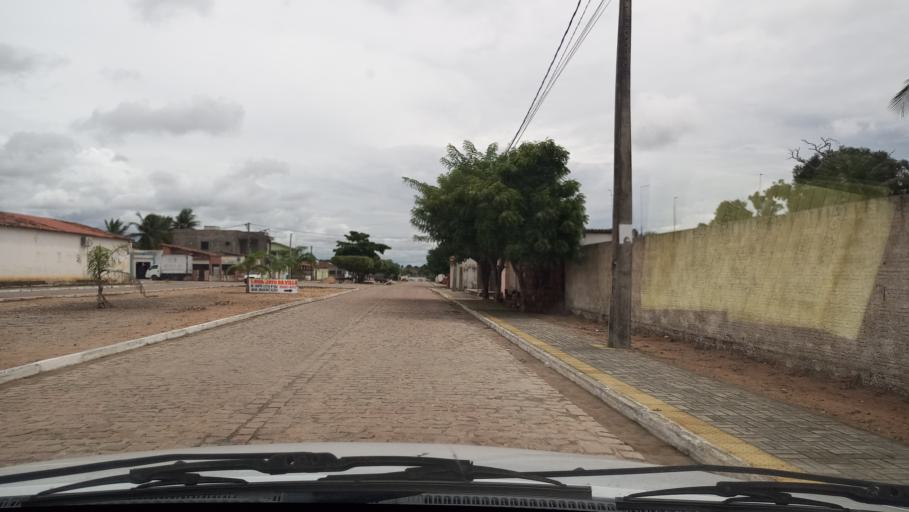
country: BR
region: Rio Grande do Norte
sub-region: Poco Branco
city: Poco Branco
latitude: -5.6185
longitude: -35.6573
